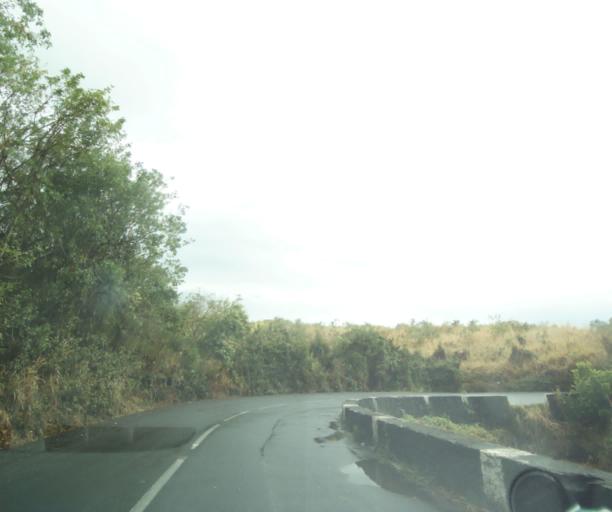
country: RE
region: Reunion
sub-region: Reunion
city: Saint-Paul
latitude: -21.0133
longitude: 55.3109
